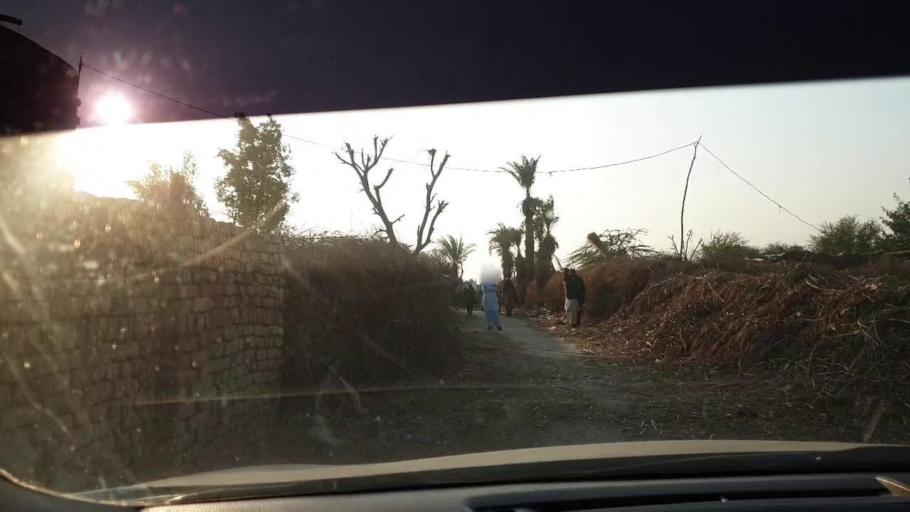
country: PK
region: Sindh
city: Berani
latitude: 25.8378
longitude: 68.8163
